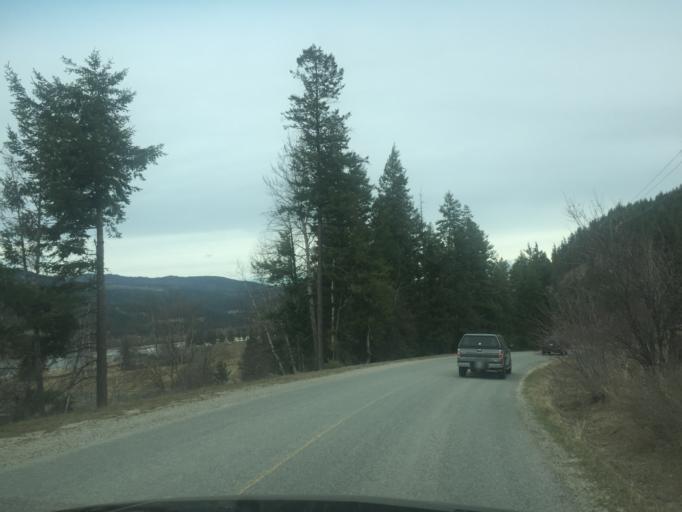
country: CA
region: British Columbia
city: Kamloops
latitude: 51.2009
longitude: -120.1358
